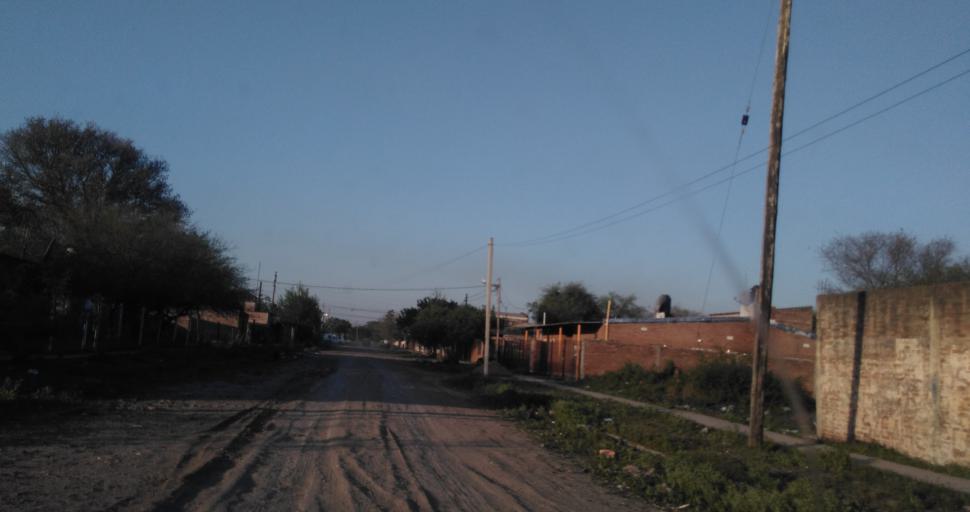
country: AR
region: Chaco
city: Resistencia
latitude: -27.4742
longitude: -59.0087
